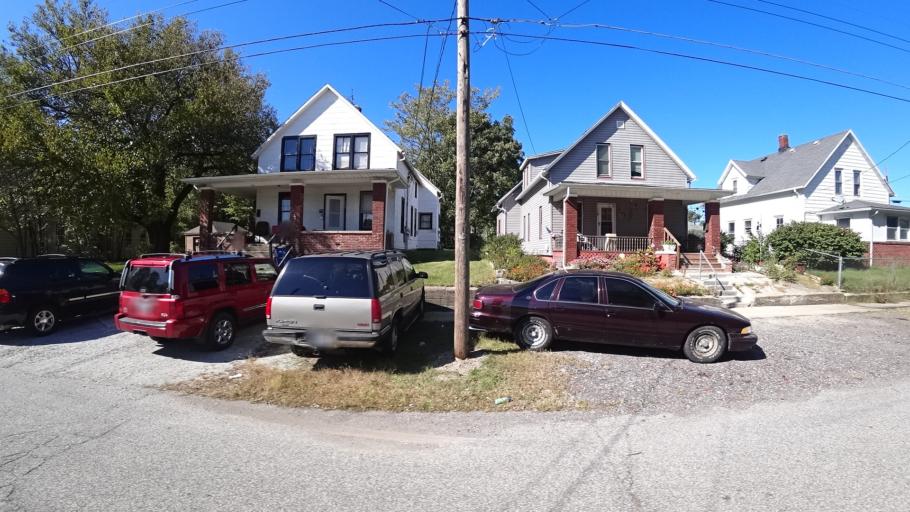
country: US
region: Indiana
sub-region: LaPorte County
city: Michigan City
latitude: 41.7108
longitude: -86.9143
